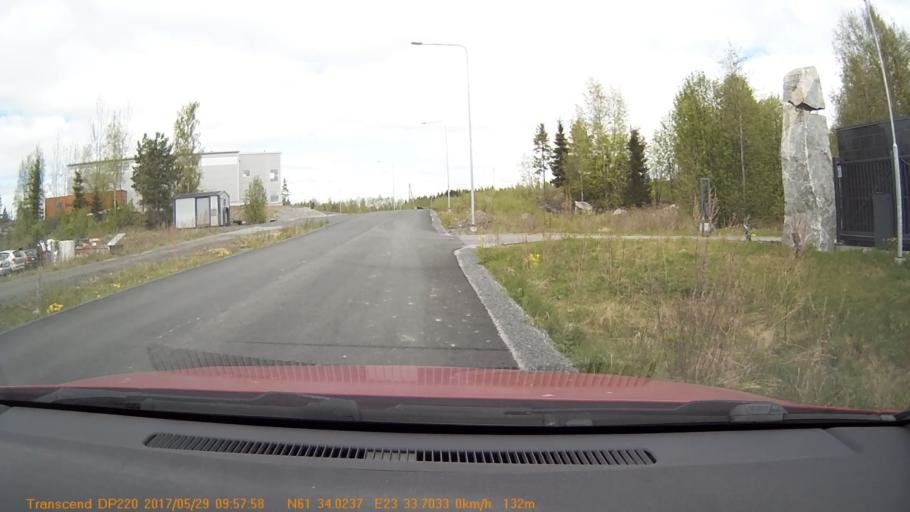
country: FI
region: Pirkanmaa
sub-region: Tampere
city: Yloejaervi
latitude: 61.5671
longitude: 23.5617
